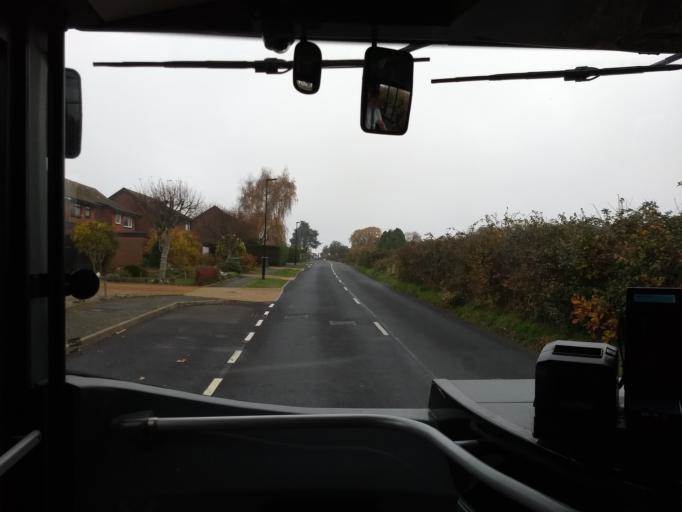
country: GB
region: England
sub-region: Isle of Wight
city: Newchurch
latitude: 50.6530
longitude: -1.2002
